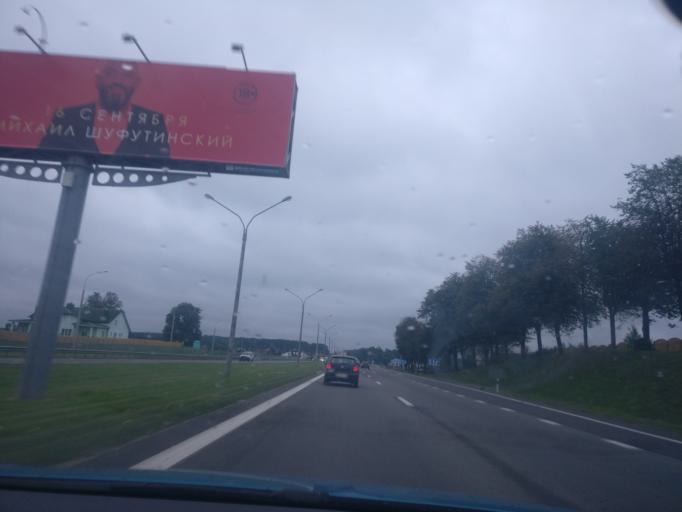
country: BY
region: Minsk
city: Korolev Stan
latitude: 53.9907
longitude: 27.8040
